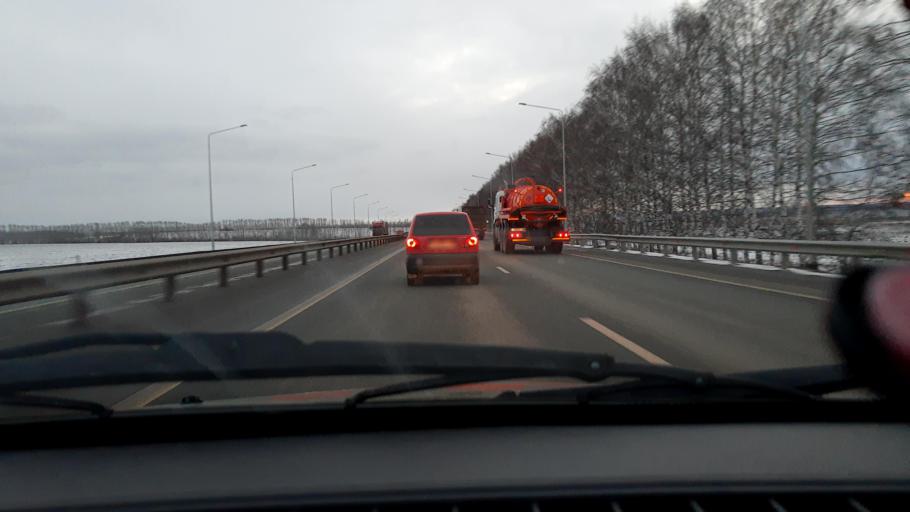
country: RU
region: Bashkortostan
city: Karmaskaly
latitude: 54.3473
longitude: 55.9066
